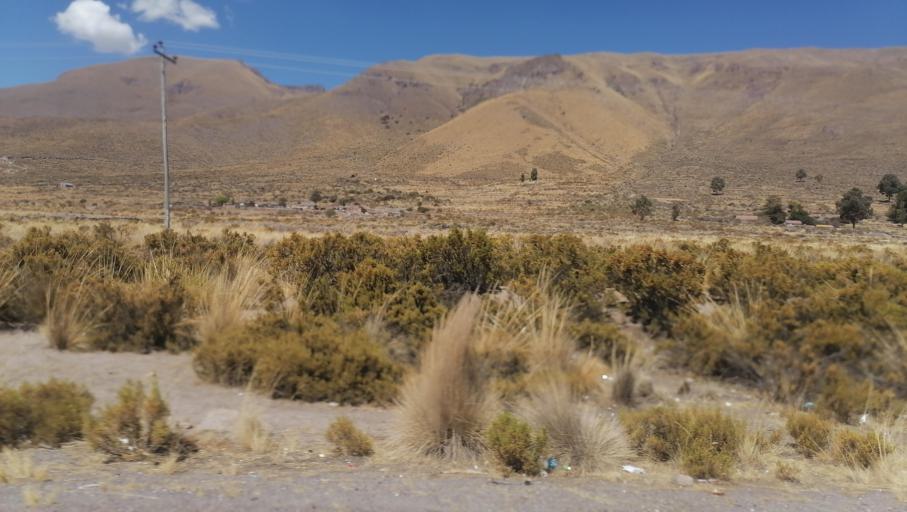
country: BO
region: Oruro
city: Challapata
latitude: -18.9848
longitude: -66.7796
